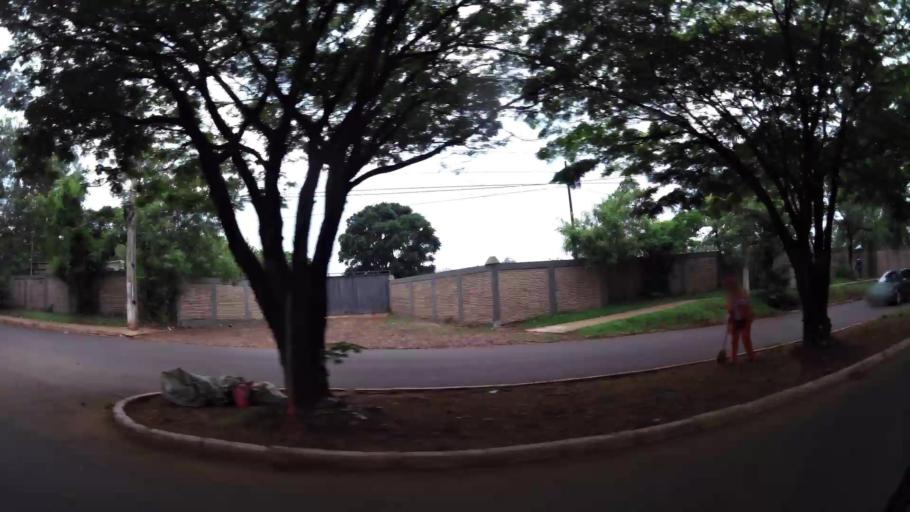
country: PY
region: Alto Parana
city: Presidente Franco
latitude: -25.5207
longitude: -54.6445
